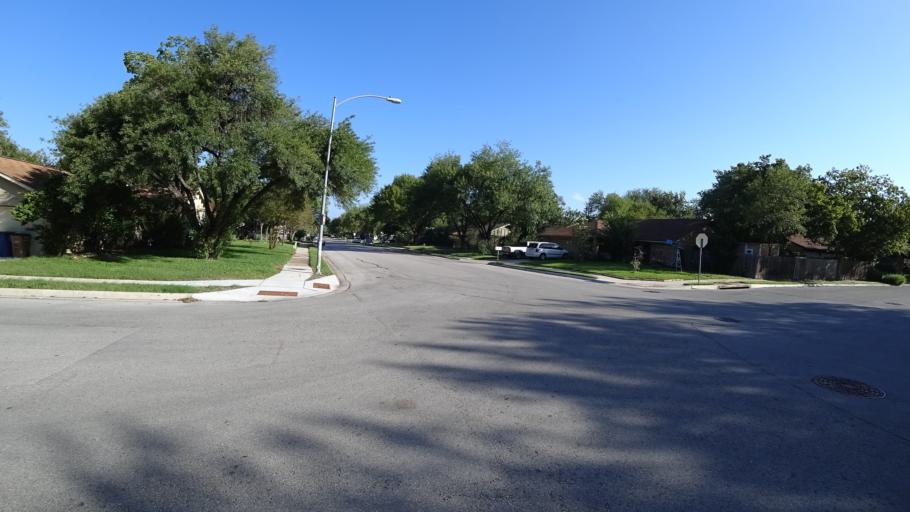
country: US
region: Texas
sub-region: Travis County
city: Shady Hollow
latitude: 30.2108
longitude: -97.8129
